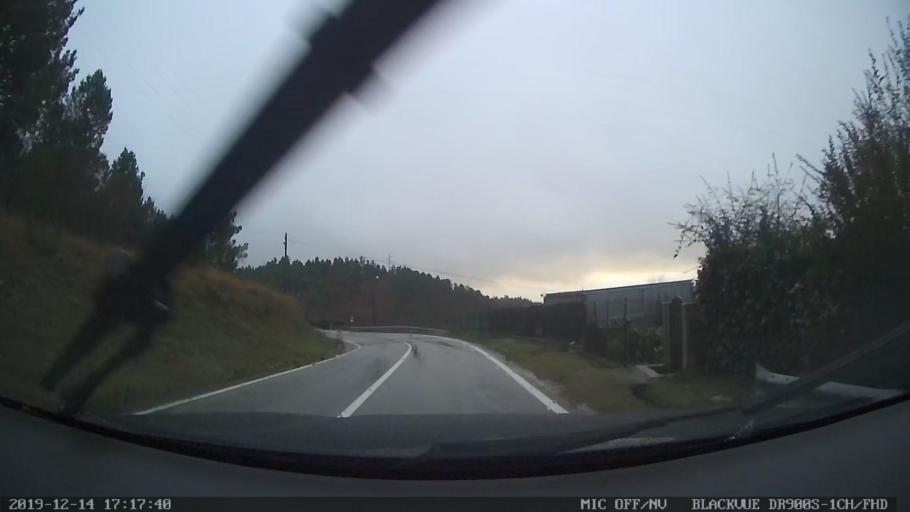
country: PT
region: Vila Real
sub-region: Vila Pouca de Aguiar
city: Vila Pouca de Aguiar
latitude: 41.4975
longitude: -7.6383
